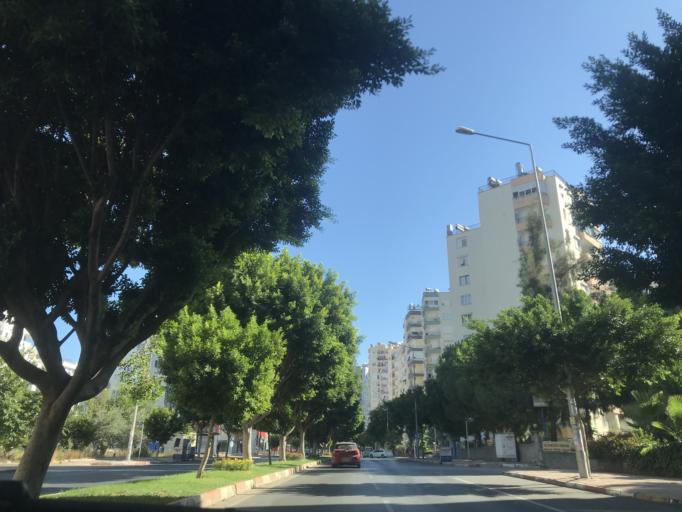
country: TR
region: Antalya
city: Antalya
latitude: 36.8964
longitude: 30.6292
